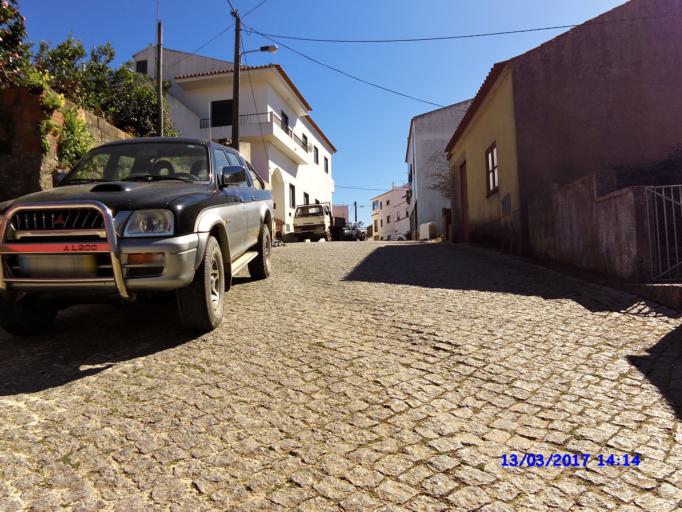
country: PT
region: Faro
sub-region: Monchique
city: Monchique
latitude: 37.3099
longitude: -8.6667
